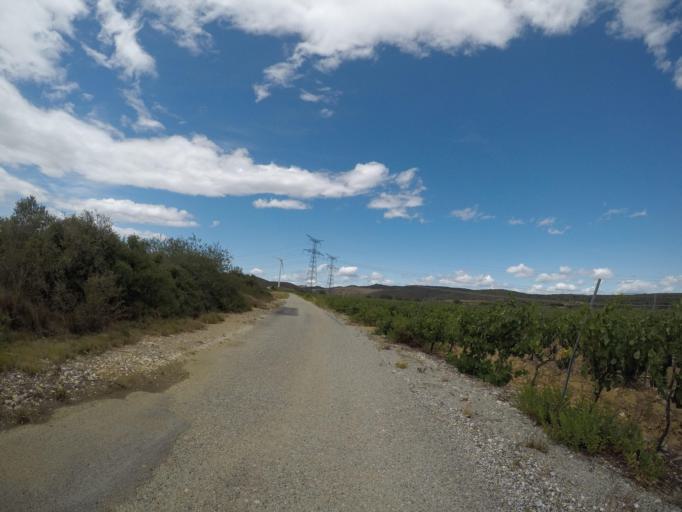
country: FR
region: Languedoc-Roussillon
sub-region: Departement des Pyrenees-Orientales
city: Pezilla-la-Riviere
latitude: 42.7194
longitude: 2.7589
